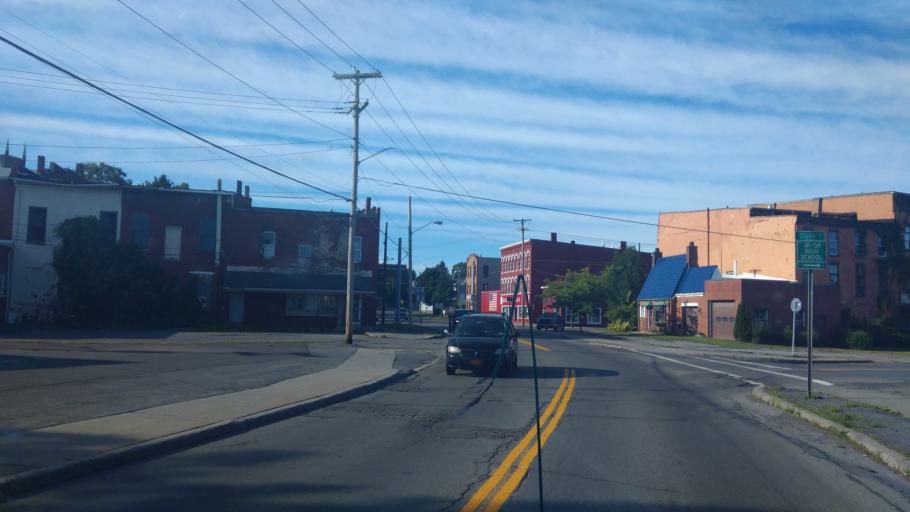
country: US
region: New York
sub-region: Wayne County
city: Lyons
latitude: 43.0635
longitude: -76.9905
